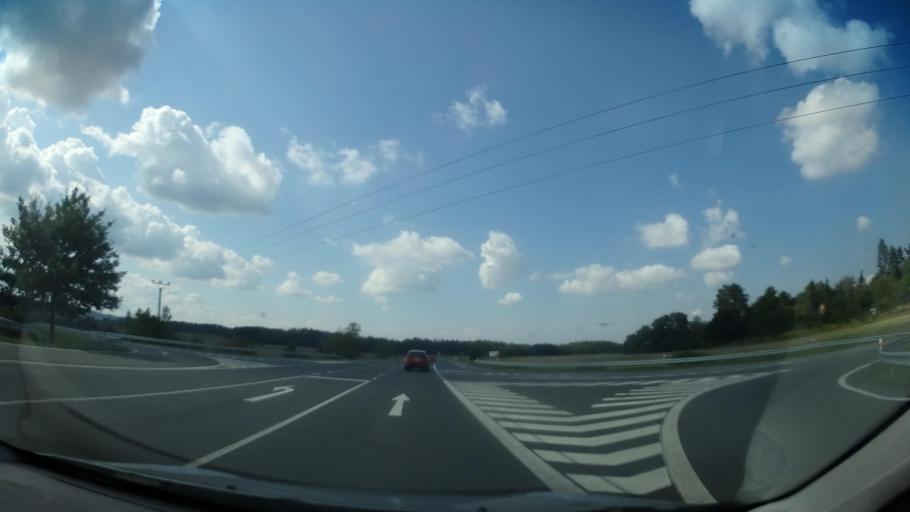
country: CZ
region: Central Bohemia
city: Kostelec nad Cernymi Lesy
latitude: 49.9850
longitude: 14.8481
